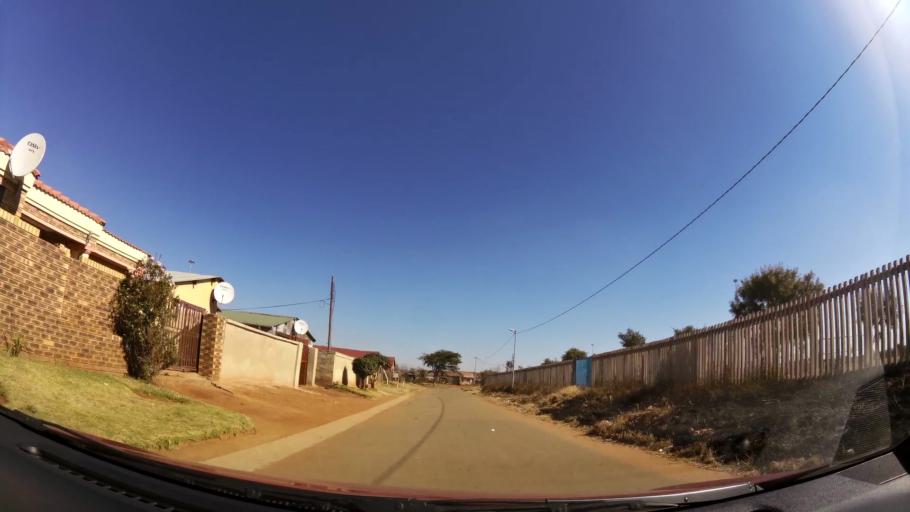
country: ZA
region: Gauteng
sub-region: City of Johannesburg Metropolitan Municipality
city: Soweto
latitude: -26.2171
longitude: 27.8269
